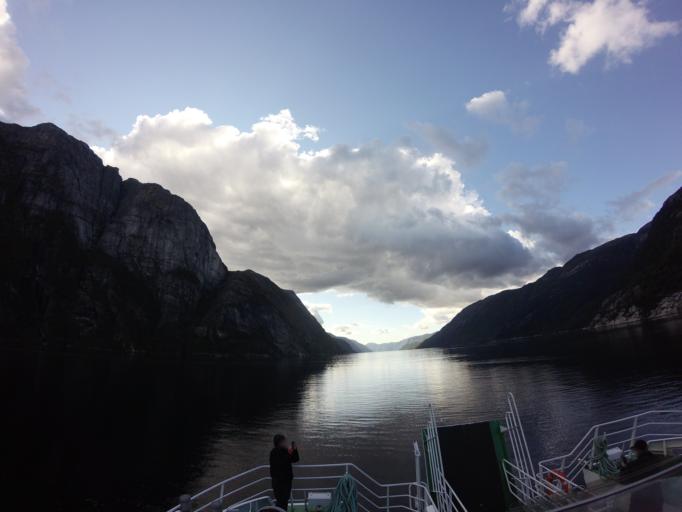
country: NO
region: Rogaland
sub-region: Hjelmeland
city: Hjelmelandsvagen
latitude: 59.0354
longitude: 6.5360
